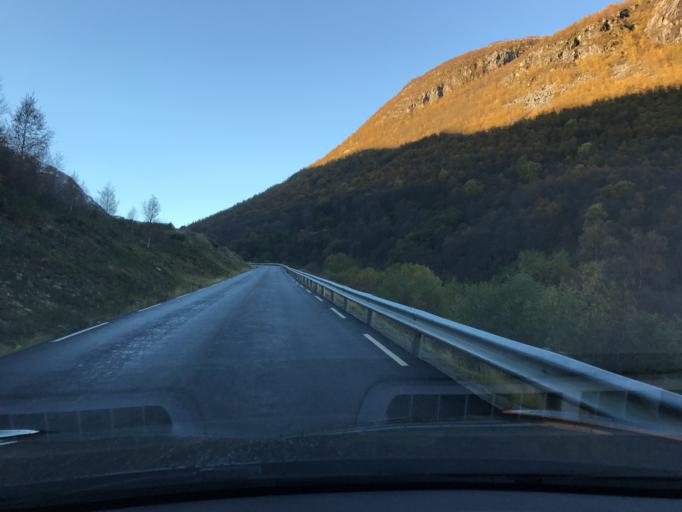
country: NO
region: Sogn og Fjordane
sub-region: Aurland
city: Aurlandsvangen
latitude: 60.8510
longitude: 7.3131
